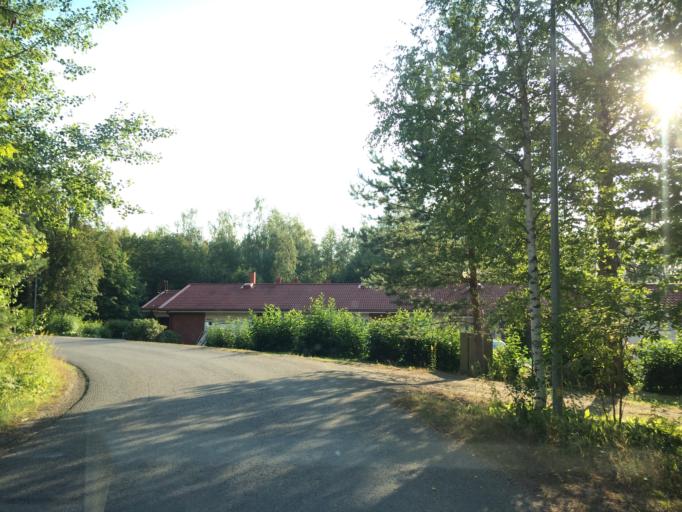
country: FI
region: Haeme
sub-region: Haemeenlinna
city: Parola
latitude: 61.0389
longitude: 24.4146
